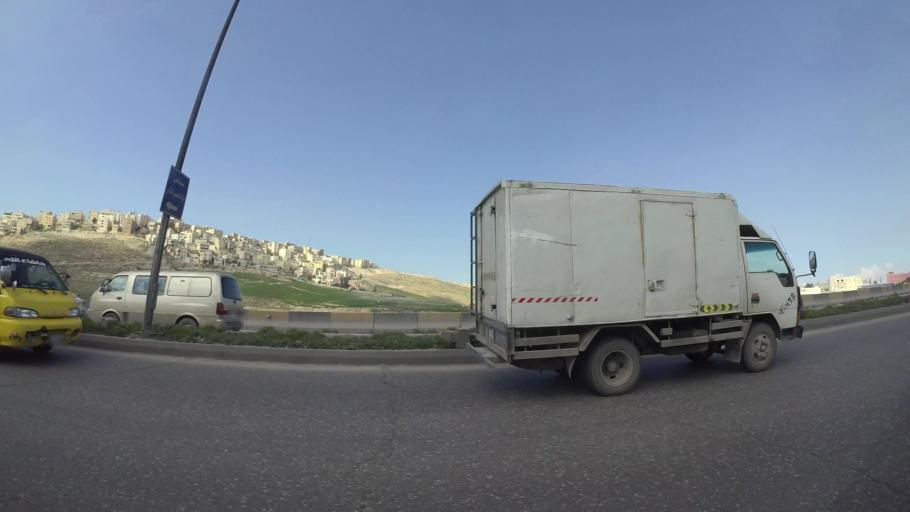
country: JO
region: Amman
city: Amman
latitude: 31.9933
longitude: 35.9843
